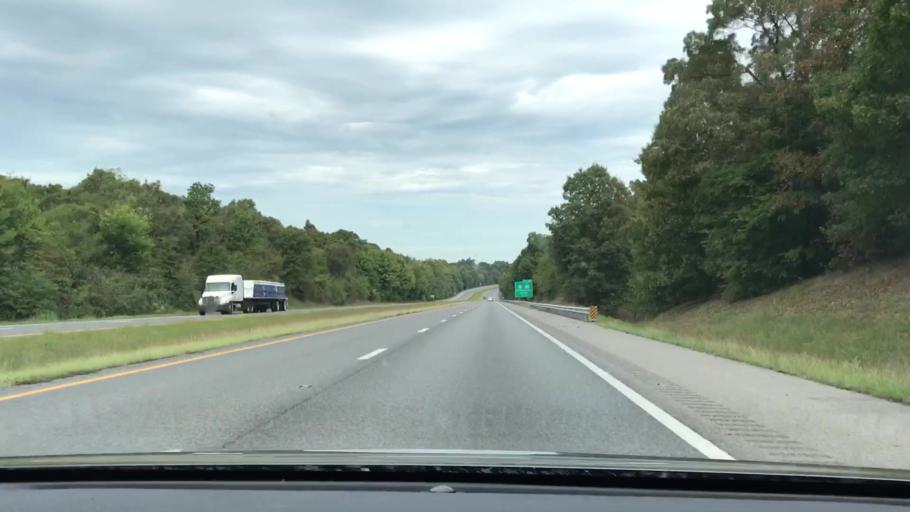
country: US
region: Kentucky
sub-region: Marshall County
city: Benton
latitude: 36.9117
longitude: -88.3495
